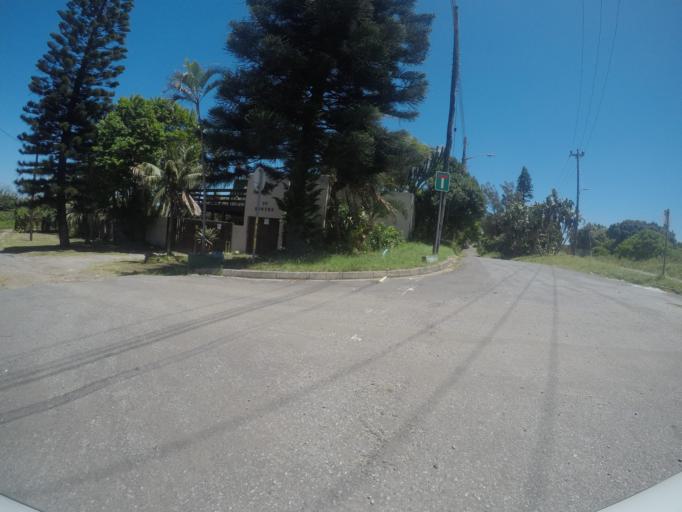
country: ZA
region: Eastern Cape
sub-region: Buffalo City Metropolitan Municipality
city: East London
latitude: -32.9554
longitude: 28.0014
